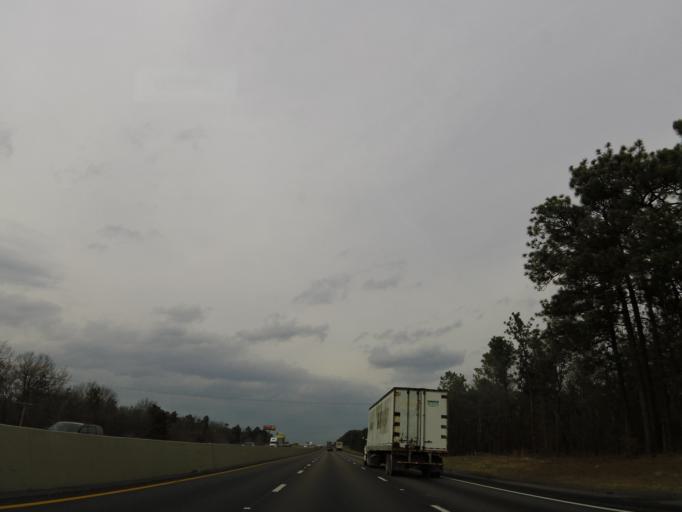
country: US
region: South Carolina
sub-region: Lexington County
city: Gaston
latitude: 33.8555
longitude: -81.0286
